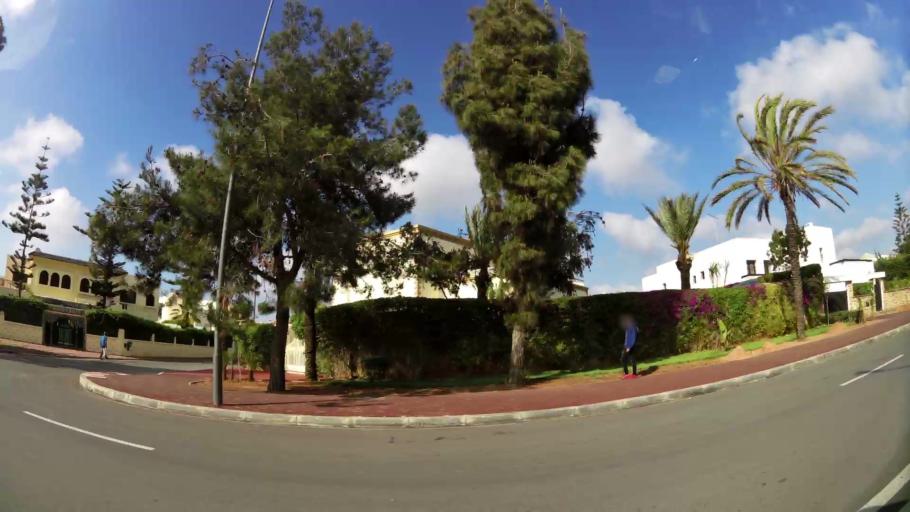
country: MA
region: Rabat-Sale-Zemmour-Zaer
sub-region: Skhirate-Temara
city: Temara
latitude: 33.9602
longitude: -6.8631
